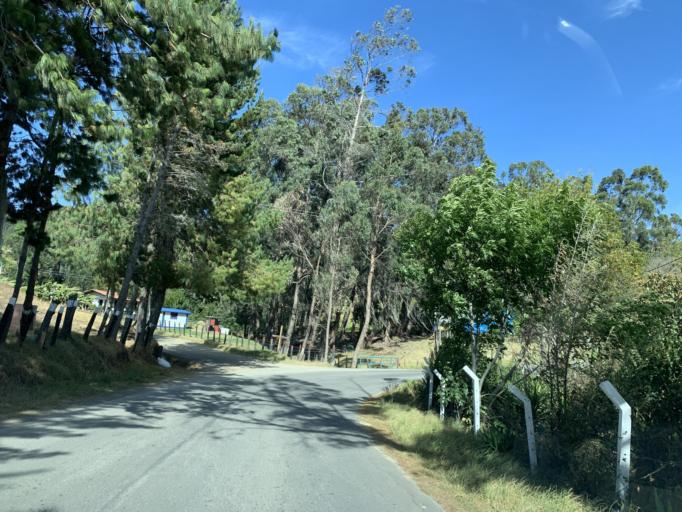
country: CO
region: Boyaca
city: Santa Sofia
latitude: 5.7083
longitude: -73.6022
